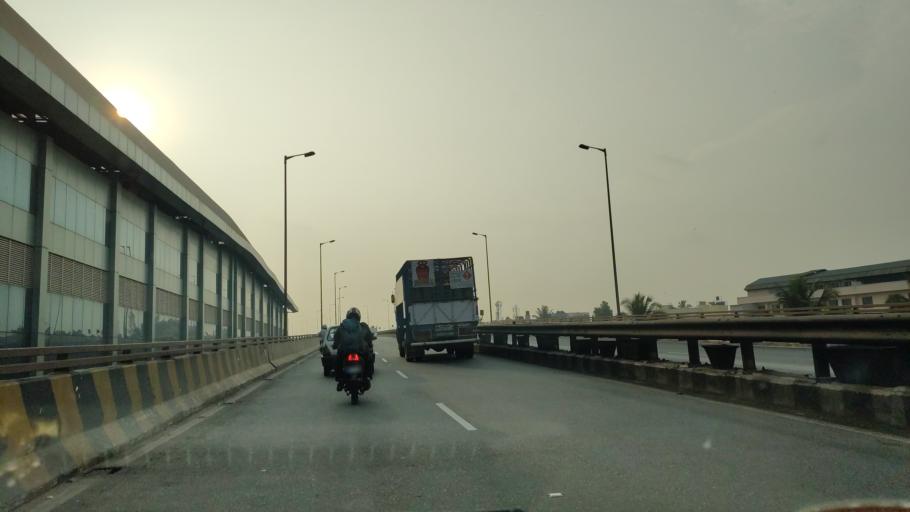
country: IN
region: Karnataka
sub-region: Bangalore Urban
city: Bangalore
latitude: 13.0364
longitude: 77.5248
